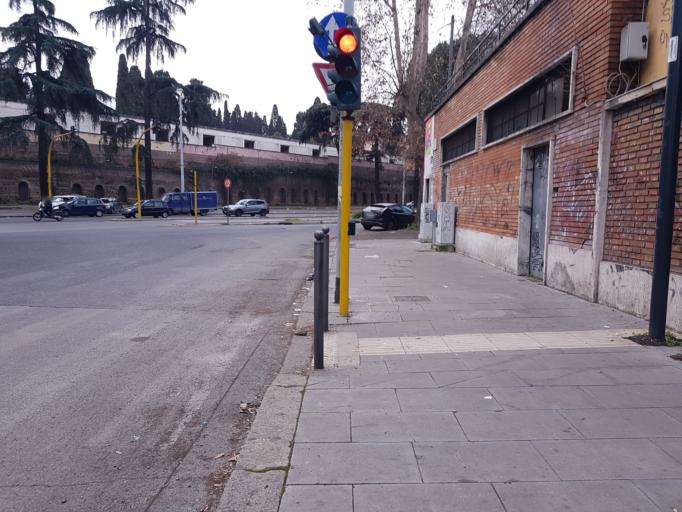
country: IT
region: Latium
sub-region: Citta metropolitana di Roma Capitale
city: Rome
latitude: 41.9056
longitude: 12.5216
